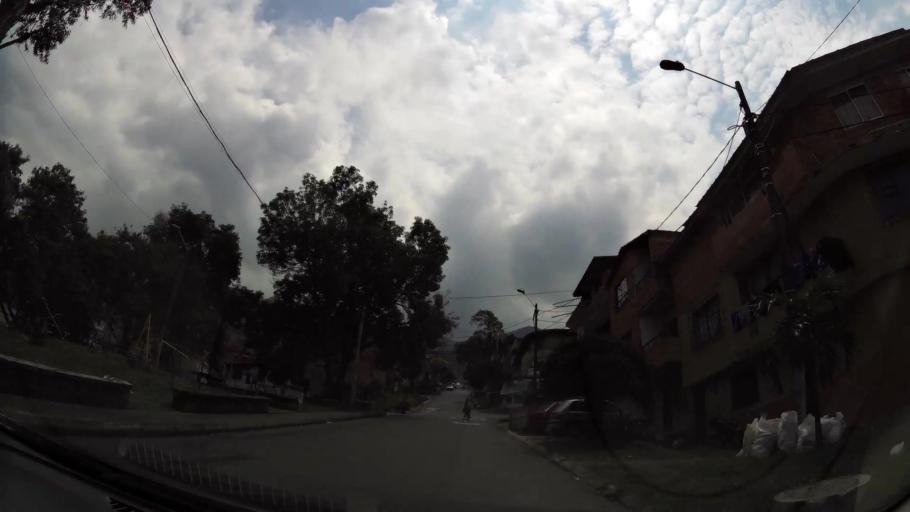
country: CO
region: Antioquia
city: Medellin
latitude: 6.2669
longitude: -75.5502
